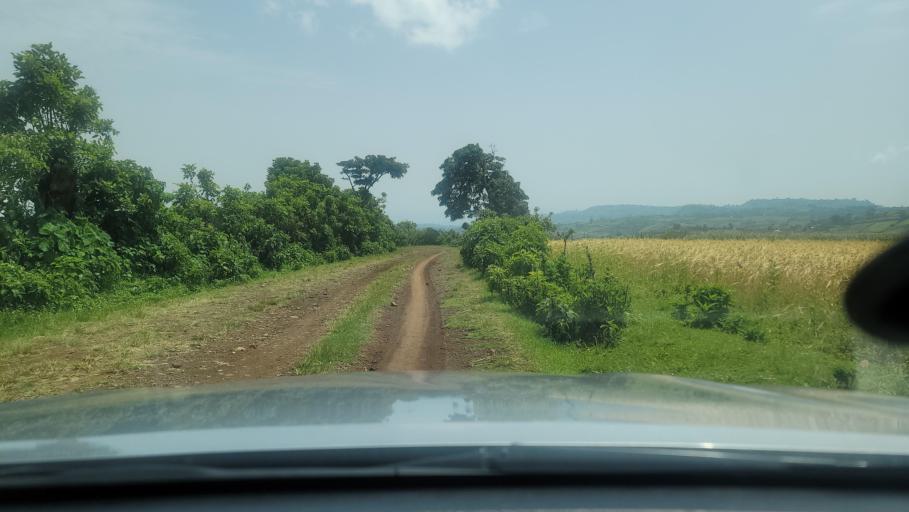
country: ET
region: Oromiya
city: Agaro
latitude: 7.8377
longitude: 36.4074
